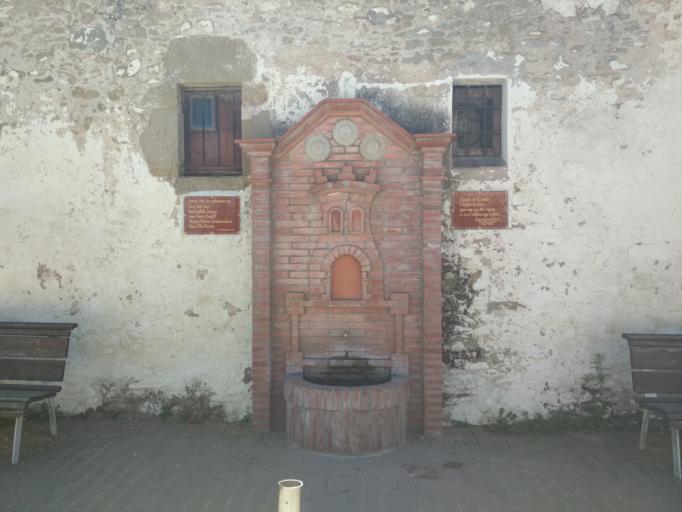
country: ES
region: Catalonia
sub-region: Provincia de Barcelona
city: Castelltercol
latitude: 41.7503
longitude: 2.1239
